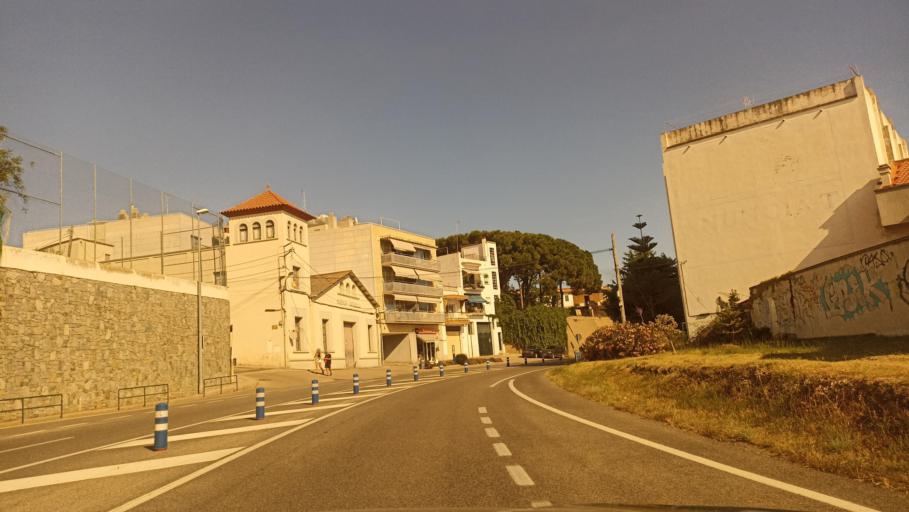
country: ES
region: Catalonia
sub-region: Provincia de Barcelona
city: Sant Pol de Mar
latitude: 41.6041
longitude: 2.6251
